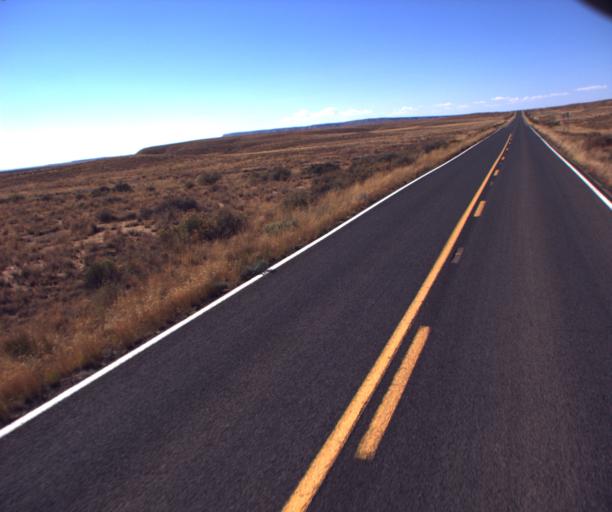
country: US
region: Arizona
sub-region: Navajo County
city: First Mesa
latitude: 35.9784
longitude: -110.7452
